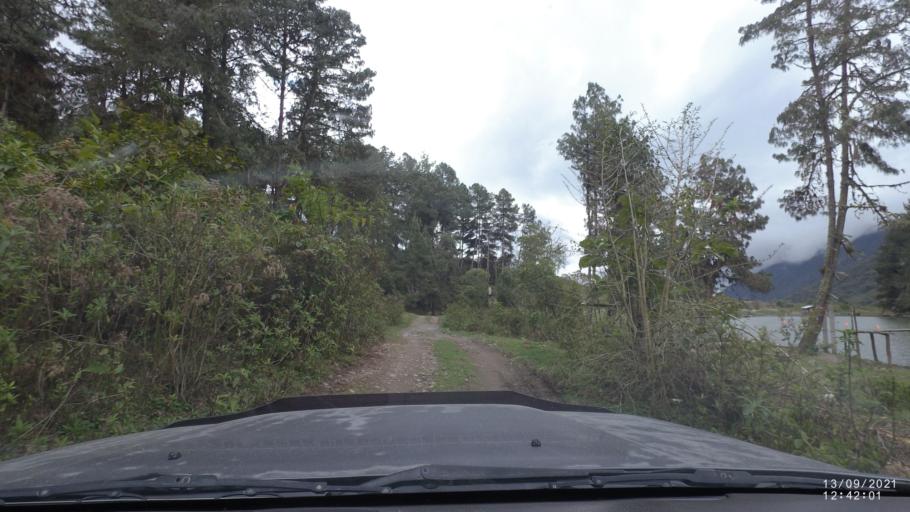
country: BO
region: Cochabamba
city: Colomi
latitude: -17.2553
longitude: -65.8175
